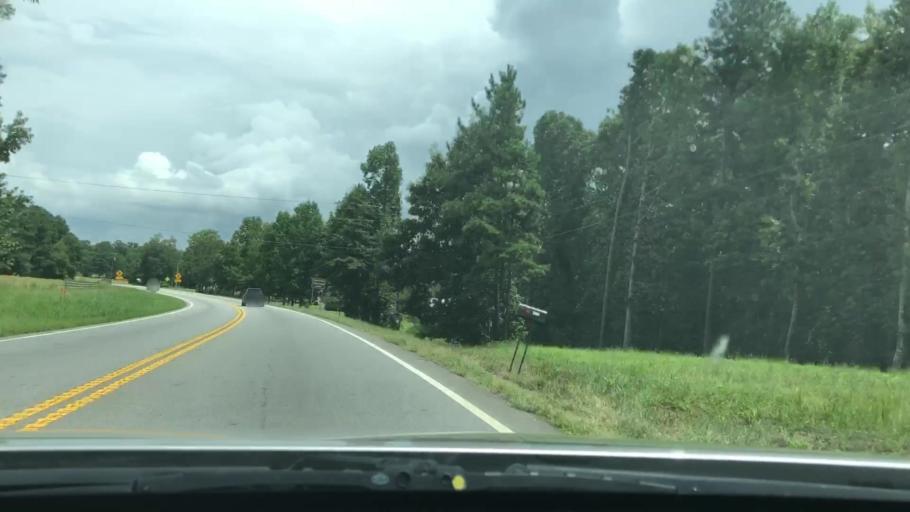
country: US
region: Georgia
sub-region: Lamar County
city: Barnesville
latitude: 33.1540
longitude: -84.1173
